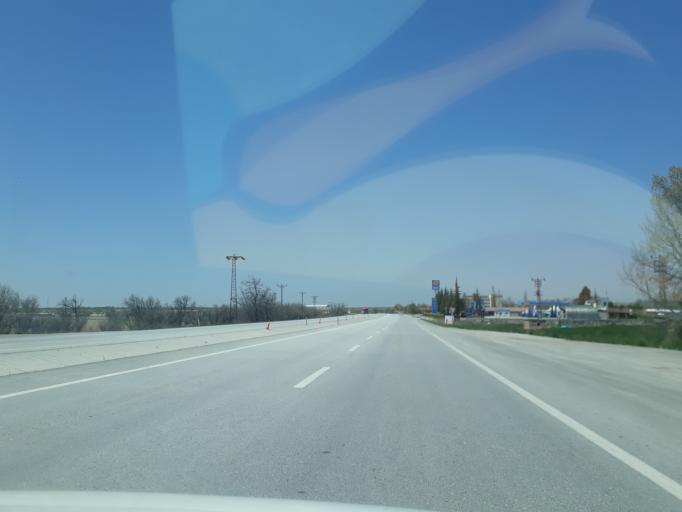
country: TR
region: Konya
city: Karapinar
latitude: 37.7163
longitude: 33.4921
